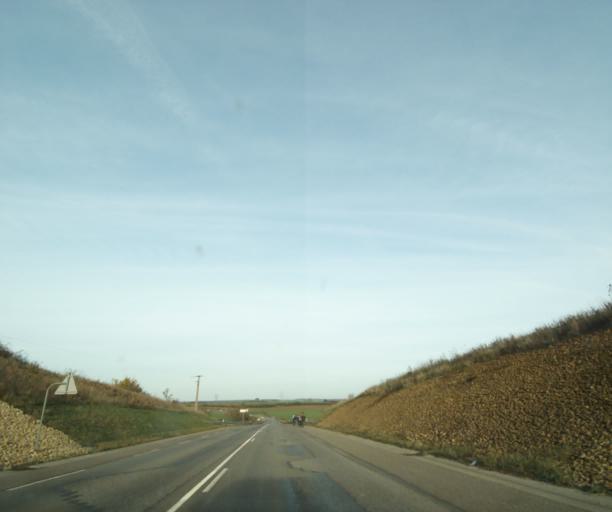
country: FR
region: Lorraine
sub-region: Departement de la Meuse
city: Etain
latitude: 49.1807
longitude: 5.6560
